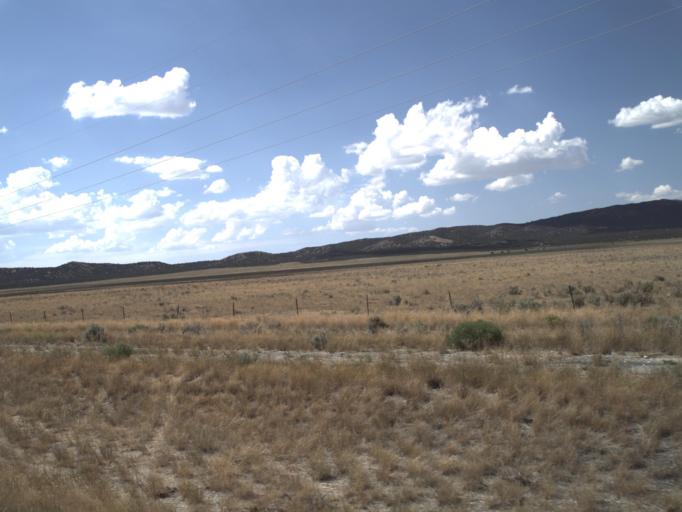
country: US
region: Idaho
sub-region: Power County
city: American Falls
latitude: 41.9690
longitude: -113.1067
